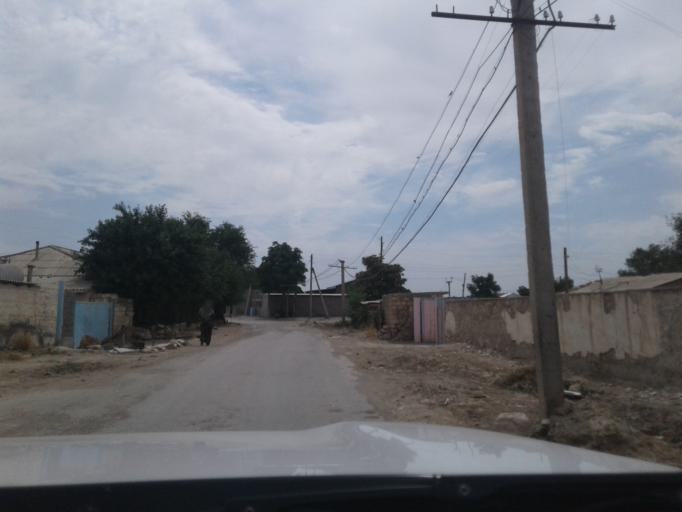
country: TM
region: Balkan
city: Serdar
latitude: 38.9891
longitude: 56.2711
